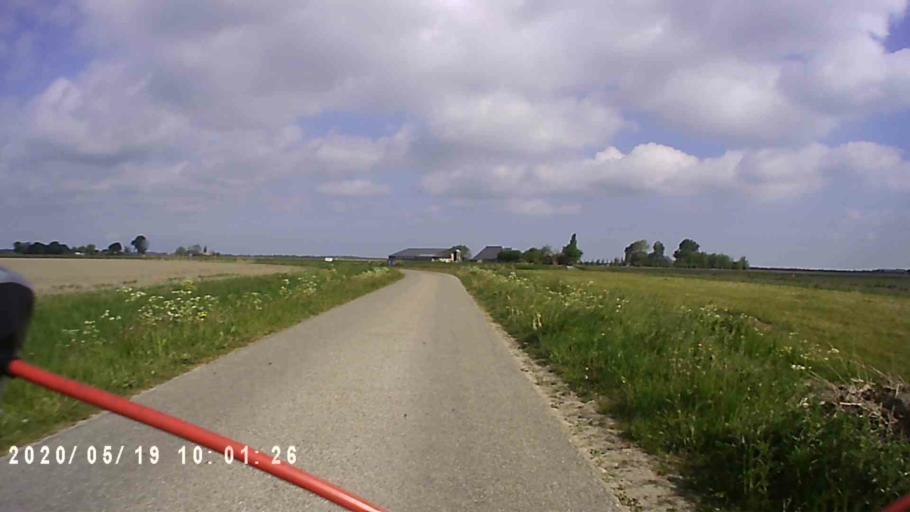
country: NL
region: Groningen
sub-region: Gemeente Zuidhorn
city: Grijpskerk
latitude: 53.3019
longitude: 6.2352
